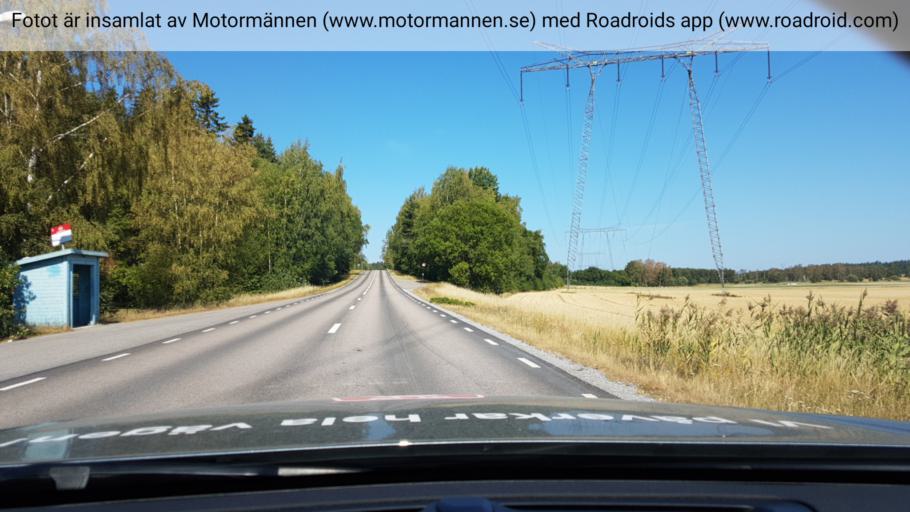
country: SE
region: Stockholm
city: Stenhamra
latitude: 59.3738
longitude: 17.6018
